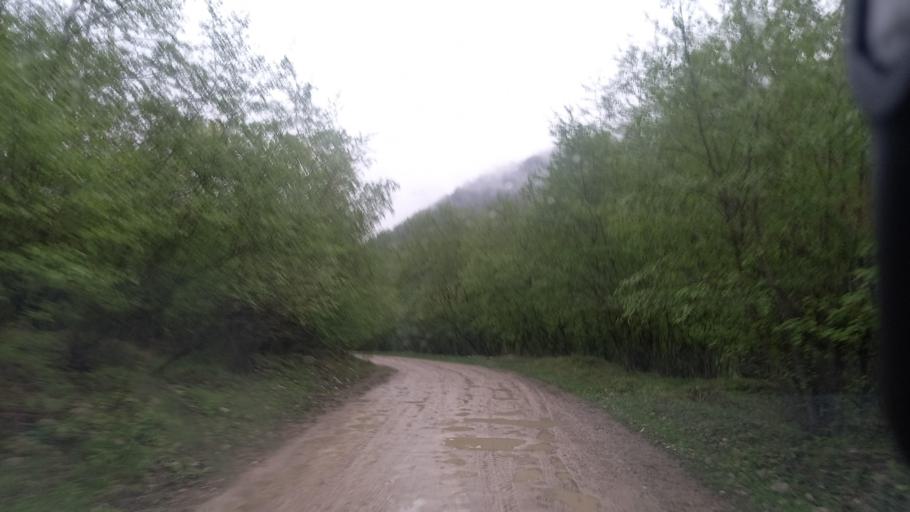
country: RU
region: Kabardino-Balkariya
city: Gundelen
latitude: 43.5978
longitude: 43.0482
